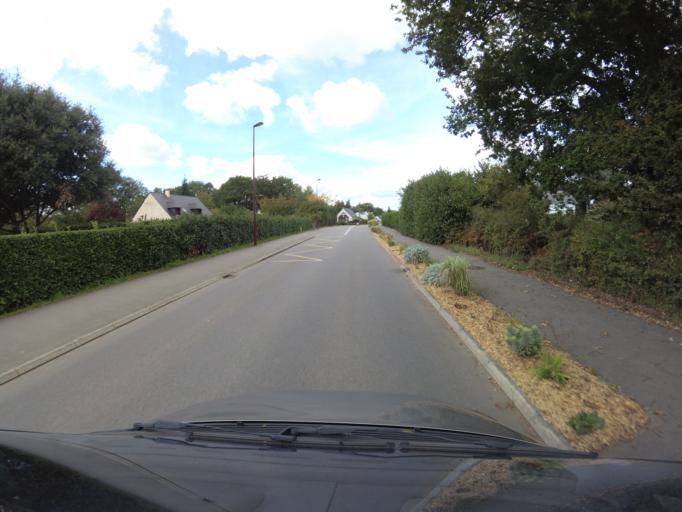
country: FR
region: Pays de la Loire
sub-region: Departement de la Loire-Atlantique
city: Suce-sur-Erdre
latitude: 47.3476
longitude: -1.5342
